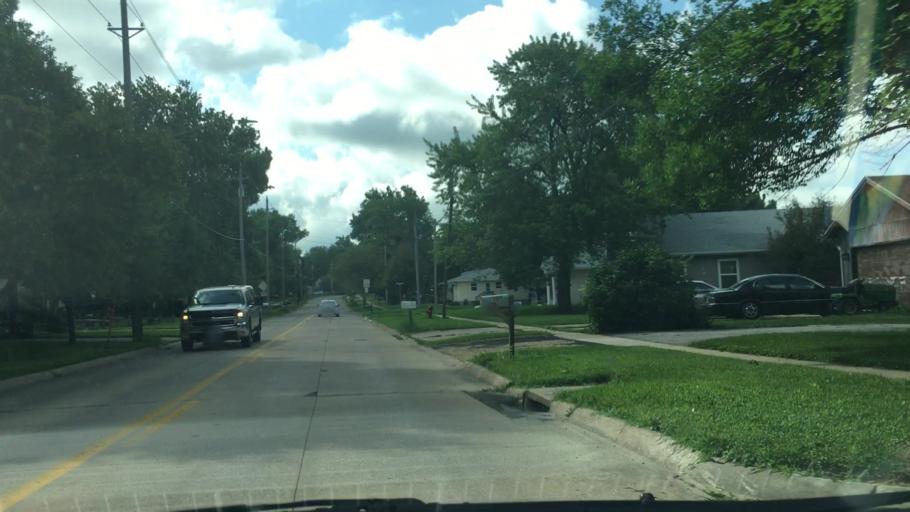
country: US
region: Iowa
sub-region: Johnson County
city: Iowa City
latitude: 41.6849
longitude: -91.5234
